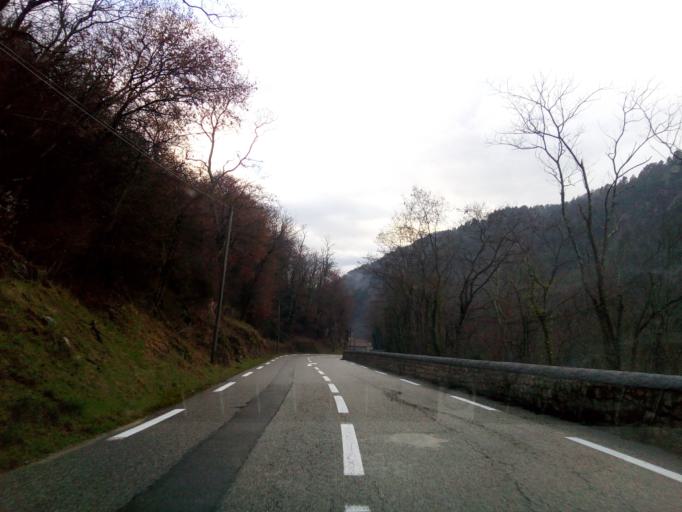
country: FR
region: Rhone-Alpes
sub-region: Departement de l'Ardeche
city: Saint-Sauveur-de-Montagut
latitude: 44.8475
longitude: 4.5720
